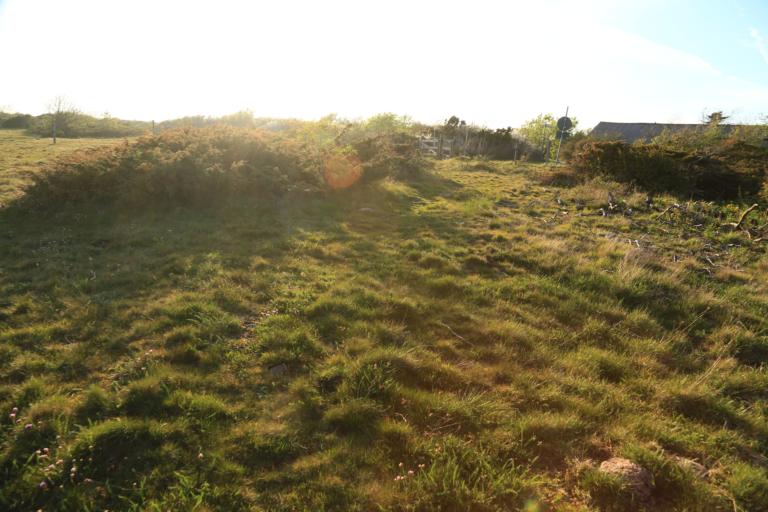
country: SE
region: Halland
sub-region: Varbergs Kommun
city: Traslovslage
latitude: 57.0362
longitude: 12.3016
